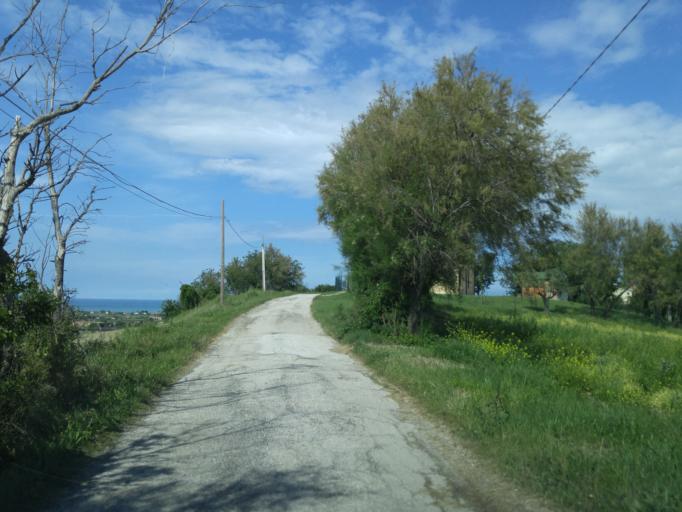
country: IT
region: The Marches
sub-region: Provincia di Pesaro e Urbino
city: San Costanzo
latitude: 43.7960
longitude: 13.0461
